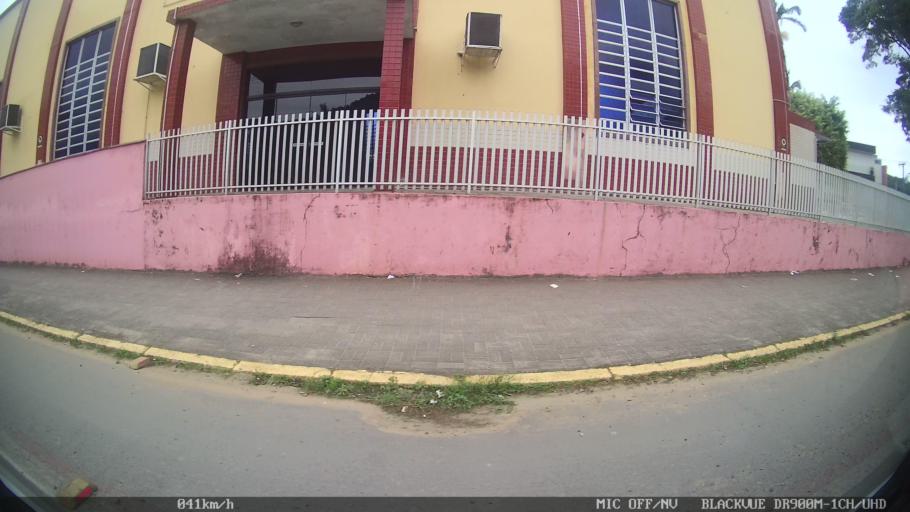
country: BR
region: Santa Catarina
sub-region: Joinville
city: Joinville
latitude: -26.2704
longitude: -48.8258
